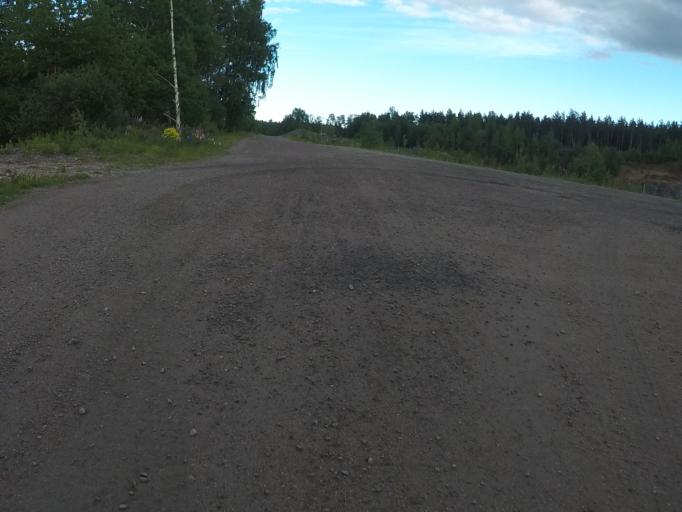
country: SE
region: Soedermanland
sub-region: Eskilstuna Kommun
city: Hallbybrunn
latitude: 59.4042
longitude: 16.4012
